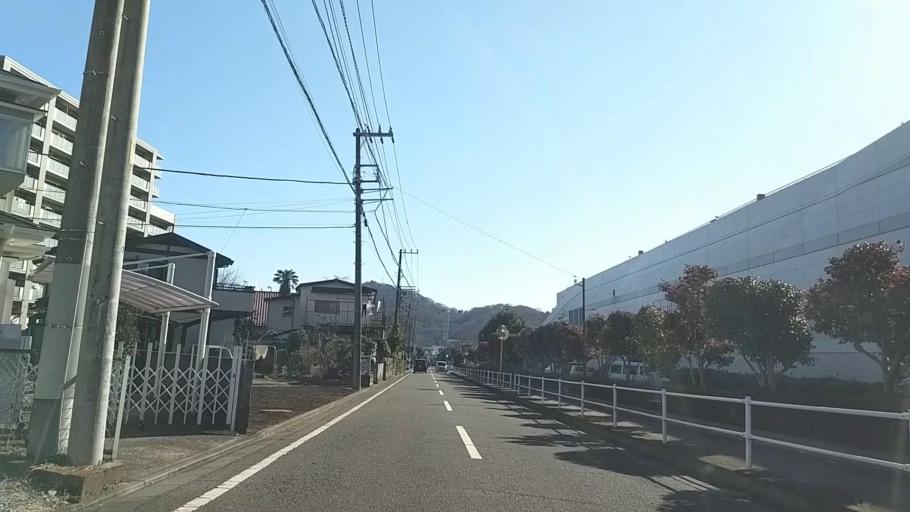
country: JP
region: Kanagawa
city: Hadano
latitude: 35.3792
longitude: 139.2281
